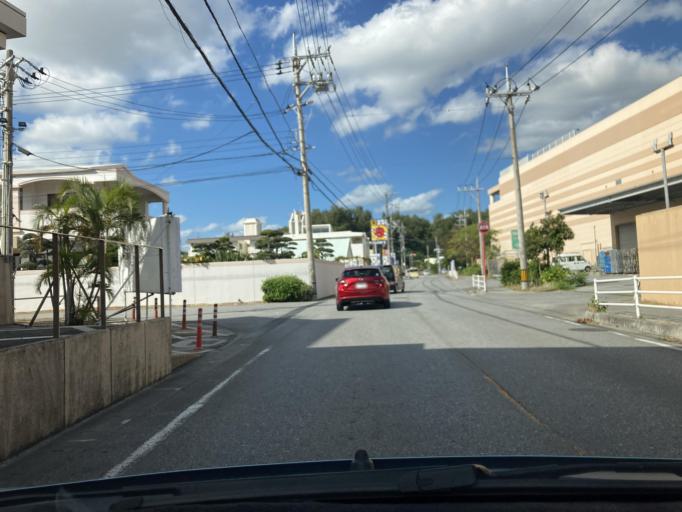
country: JP
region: Okinawa
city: Katsuren-haebaru
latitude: 26.3371
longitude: 127.8437
